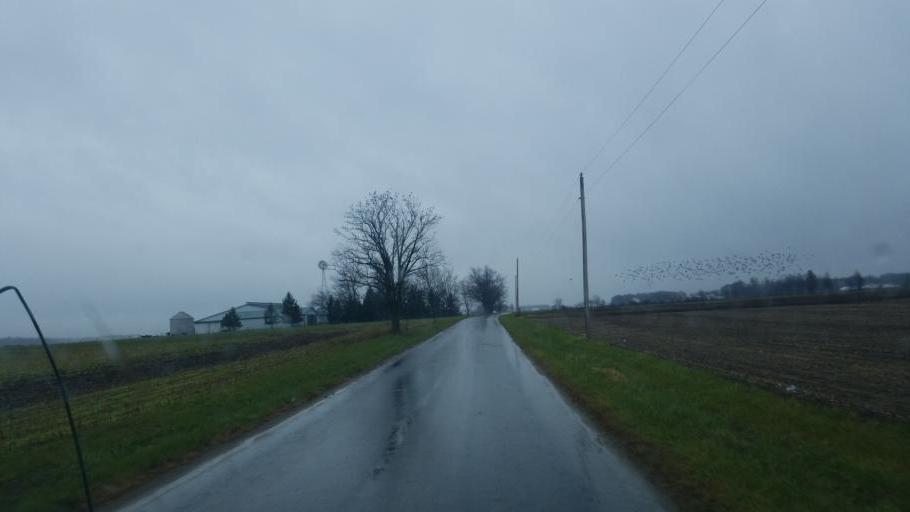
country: US
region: Indiana
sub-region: Adams County
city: Berne
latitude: 40.6378
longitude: -84.8781
